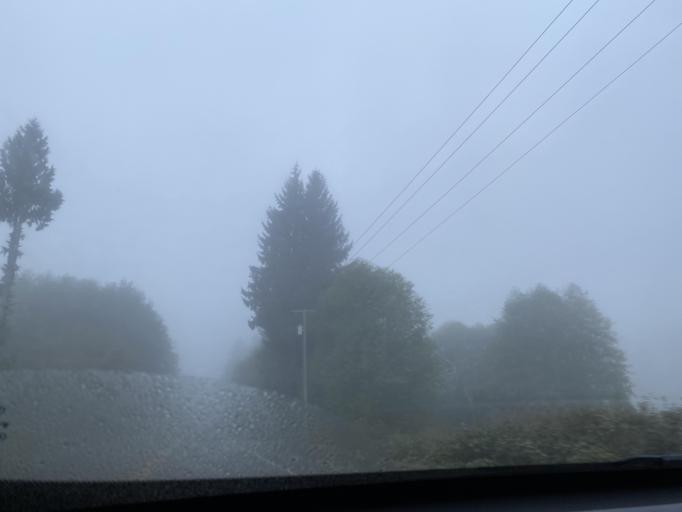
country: US
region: Washington
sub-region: Clallam County
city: Forks
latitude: 47.9348
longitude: -124.4026
